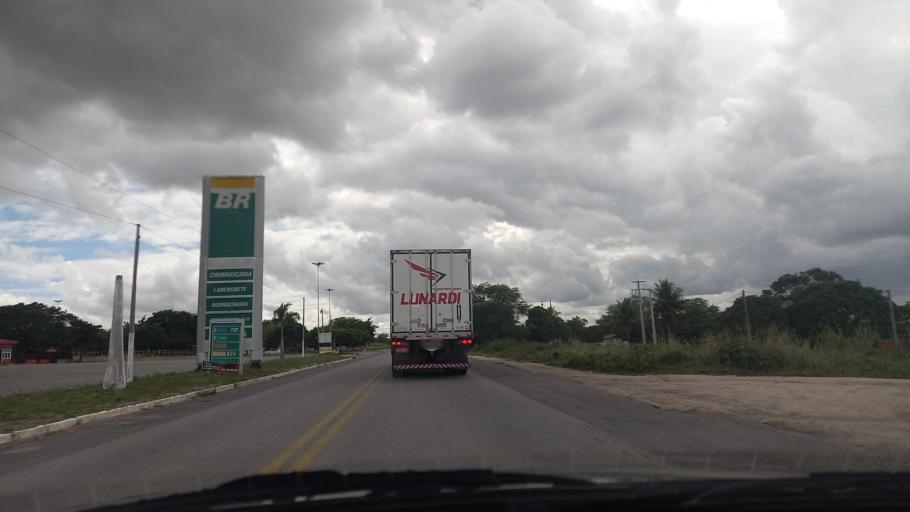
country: BR
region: Pernambuco
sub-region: Lajedo
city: Lajedo
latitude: -8.6665
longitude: -36.3665
